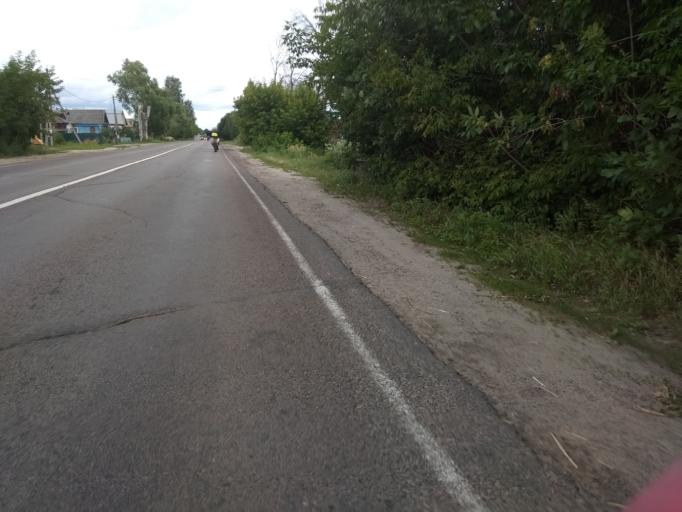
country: RU
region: Moskovskaya
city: Kerva
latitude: 55.5952
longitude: 39.7026
